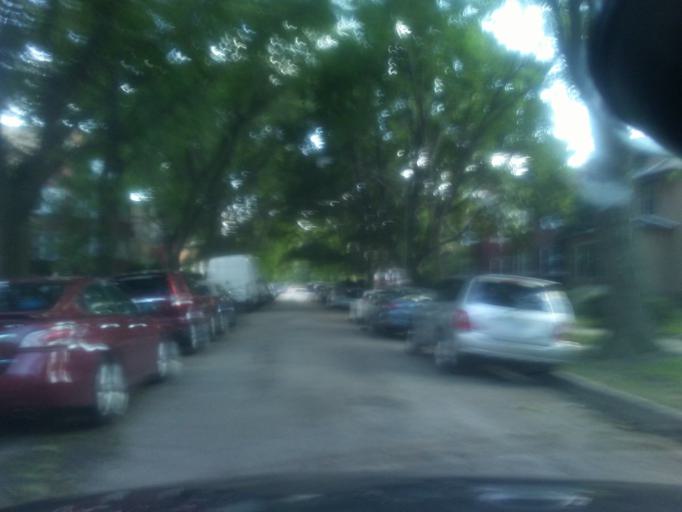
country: US
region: Illinois
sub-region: Cook County
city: Lincolnwood
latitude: 41.9714
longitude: -87.7208
